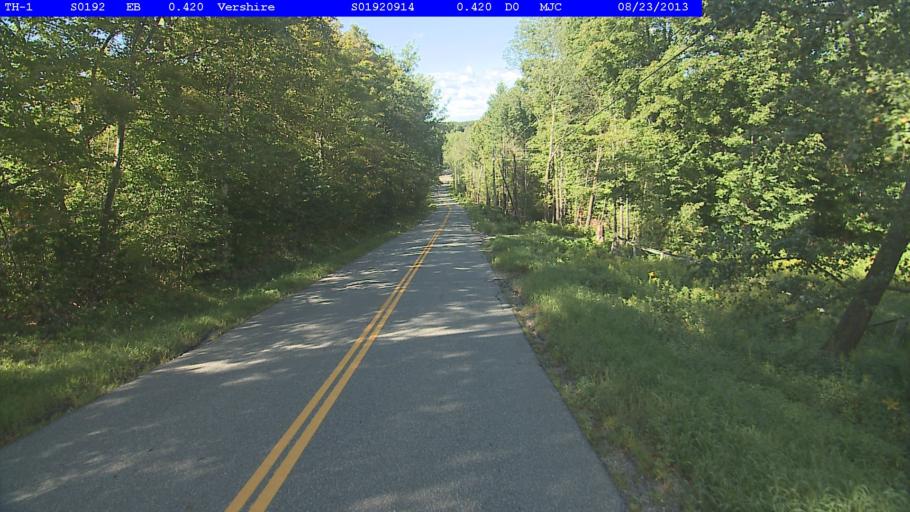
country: US
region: Vermont
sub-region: Orange County
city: Chelsea
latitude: 43.9928
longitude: -72.3658
